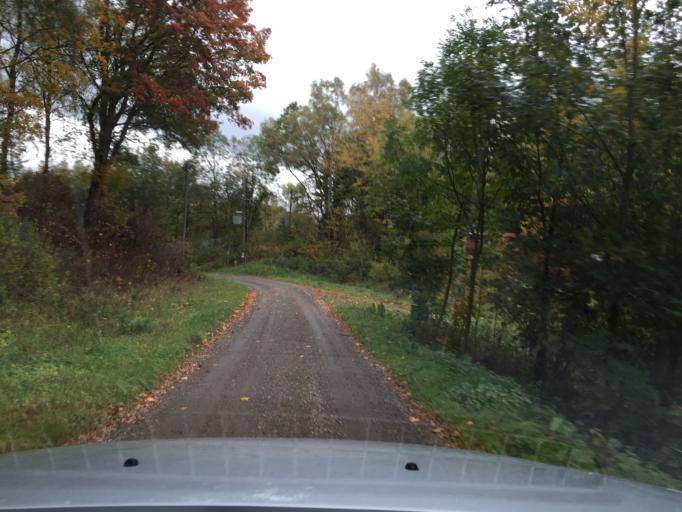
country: SE
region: Skane
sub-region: Hassleholms Kommun
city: Tormestorp
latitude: 56.0681
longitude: 13.7534
